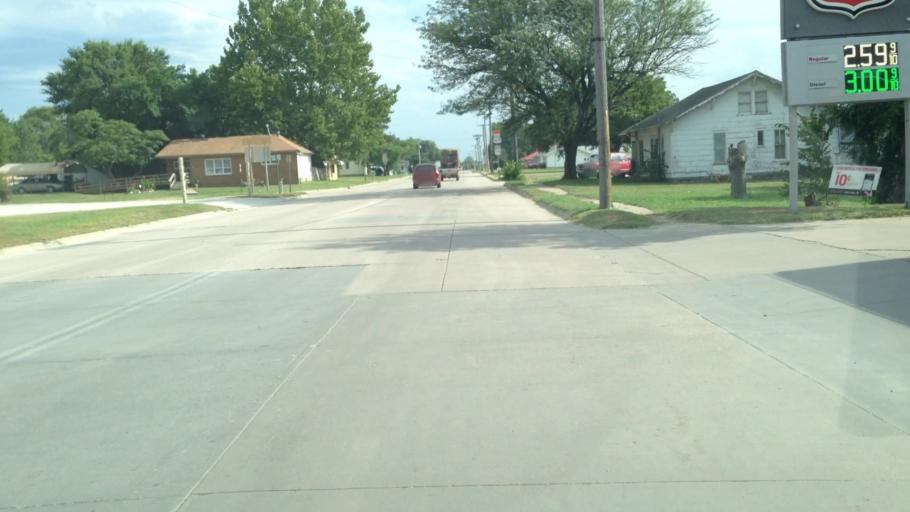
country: US
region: Kansas
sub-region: Woodson County
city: Yates Center
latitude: 37.8789
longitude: -95.7389
